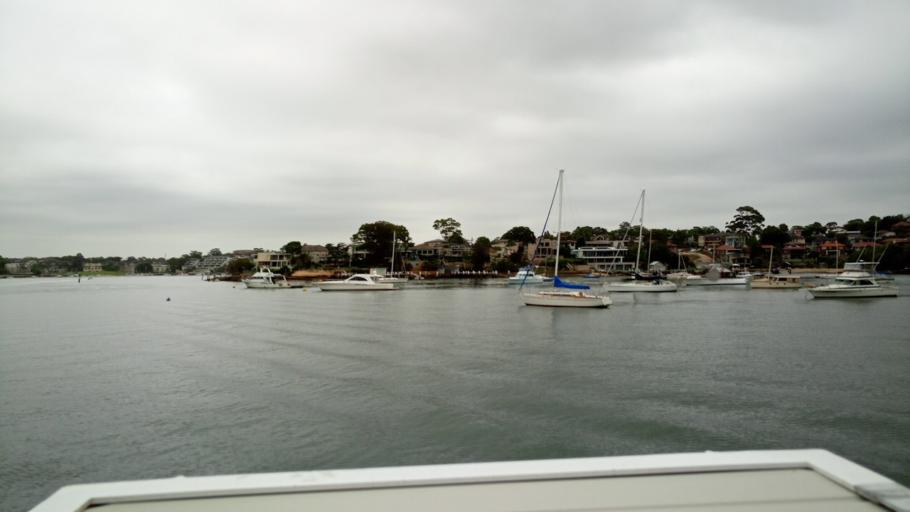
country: AU
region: New South Wales
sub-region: Hunters Hill
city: Hunters Hill
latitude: -33.8430
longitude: 151.1414
